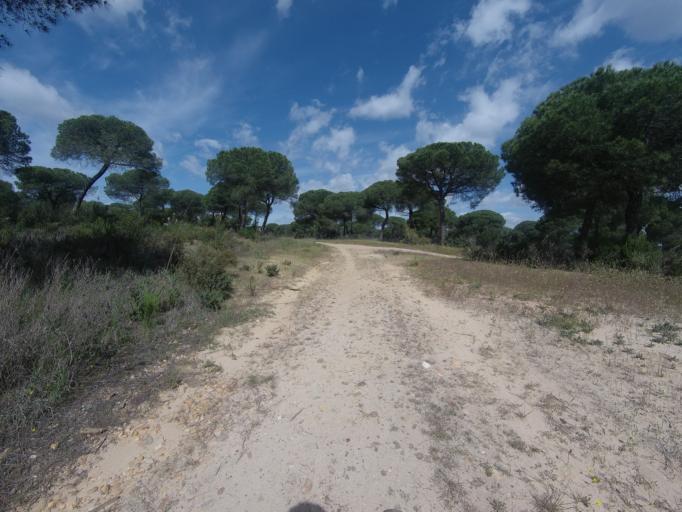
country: ES
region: Andalusia
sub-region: Provincia de Huelva
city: Aljaraque
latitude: 37.2337
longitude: -7.0621
